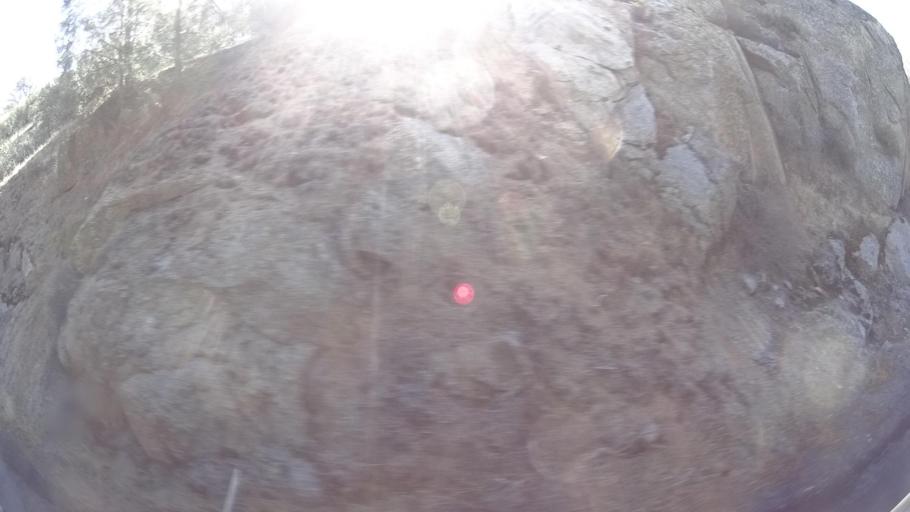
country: US
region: California
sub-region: Kern County
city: Bodfish
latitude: 35.5939
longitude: -118.5095
